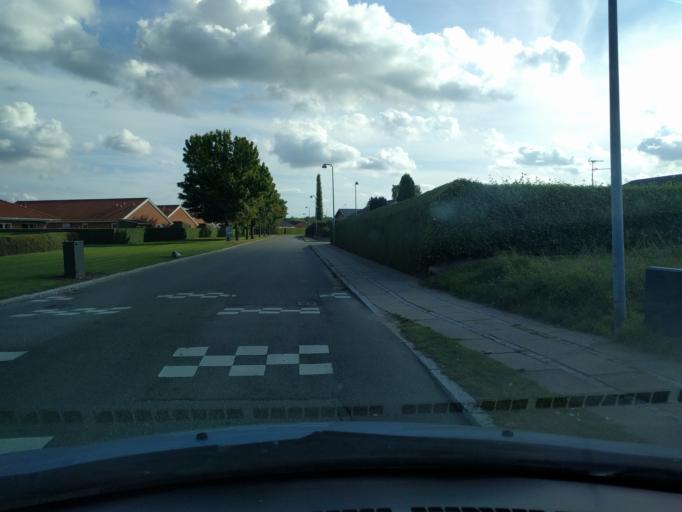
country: DK
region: South Denmark
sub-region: Odense Kommune
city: Neder Holluf
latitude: 55.3589
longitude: 10.4995
